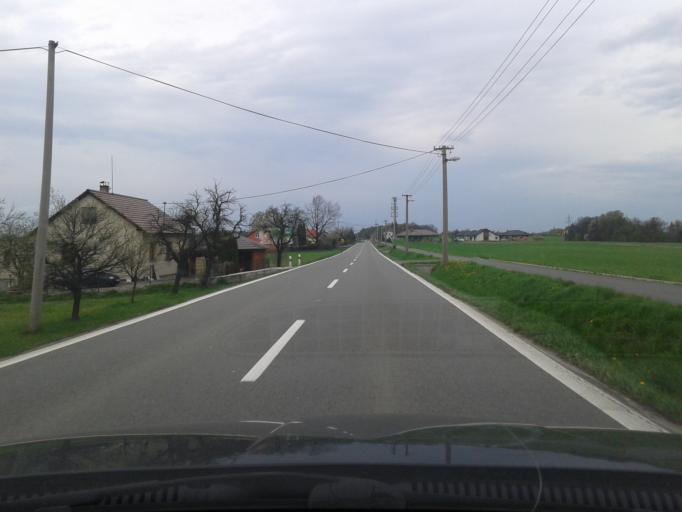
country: CZ
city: Sedliste
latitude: 49.7238
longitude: 18.3675
